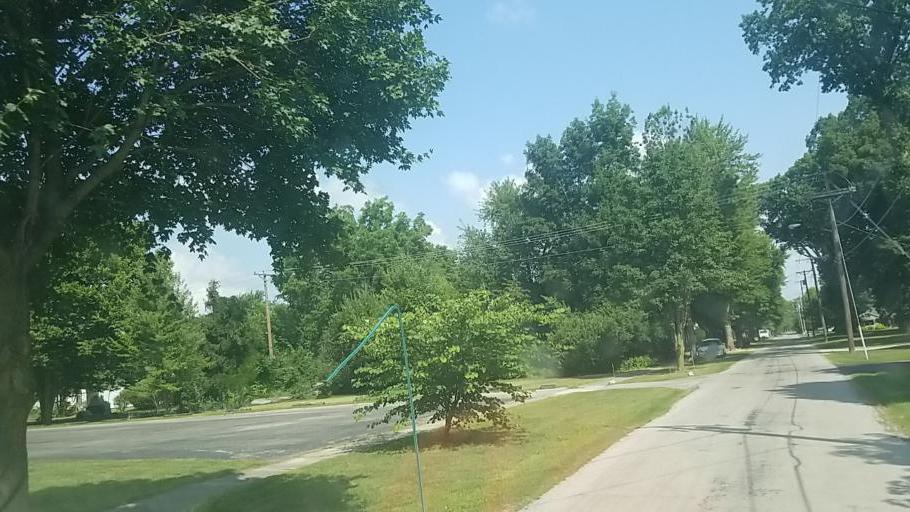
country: US
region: Ohio
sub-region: Wyandot County
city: Upper Sandusky
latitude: 40.8153
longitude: -83.2829
